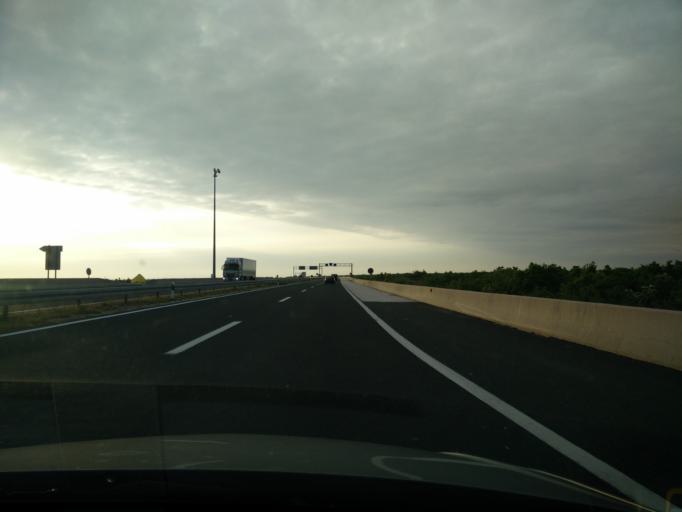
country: HR
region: Zadarska
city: Galovac
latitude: 44.1153
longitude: 15.4437
